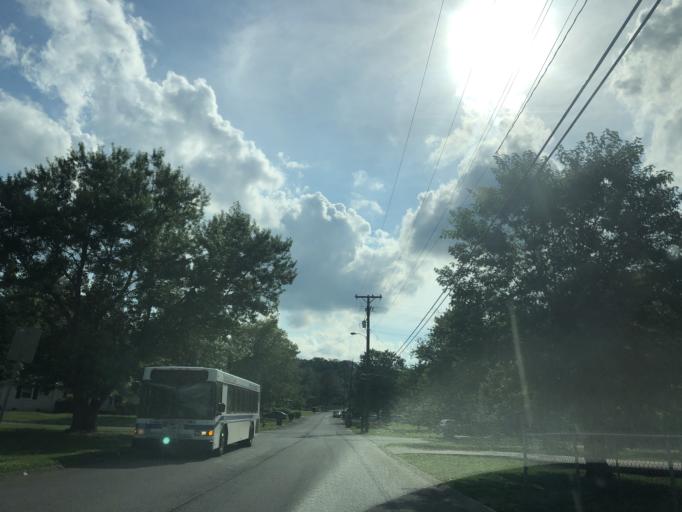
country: US
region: Tennessee
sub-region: Davidson County
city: Nashville
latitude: 36.2281
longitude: -86.8269
